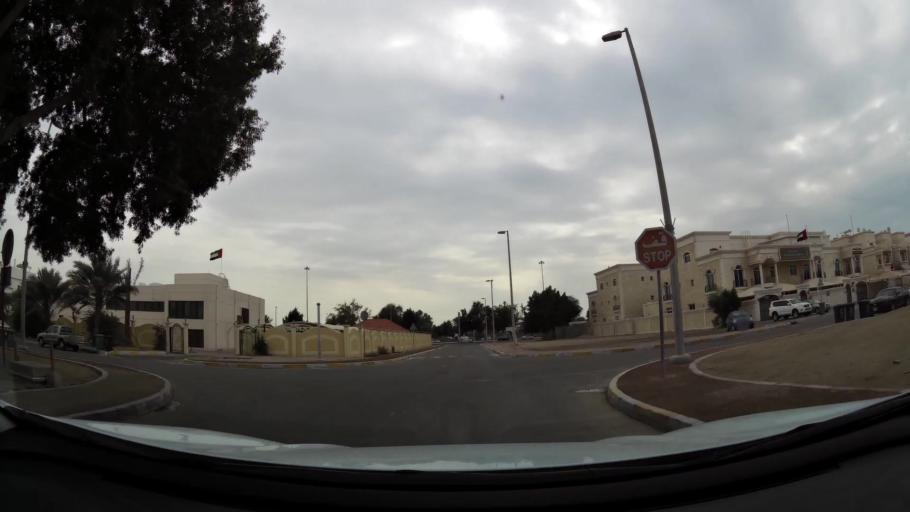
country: AE
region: Abu Dhabi
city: Abu Dhabi
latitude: 24.4277
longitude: 54.4044
